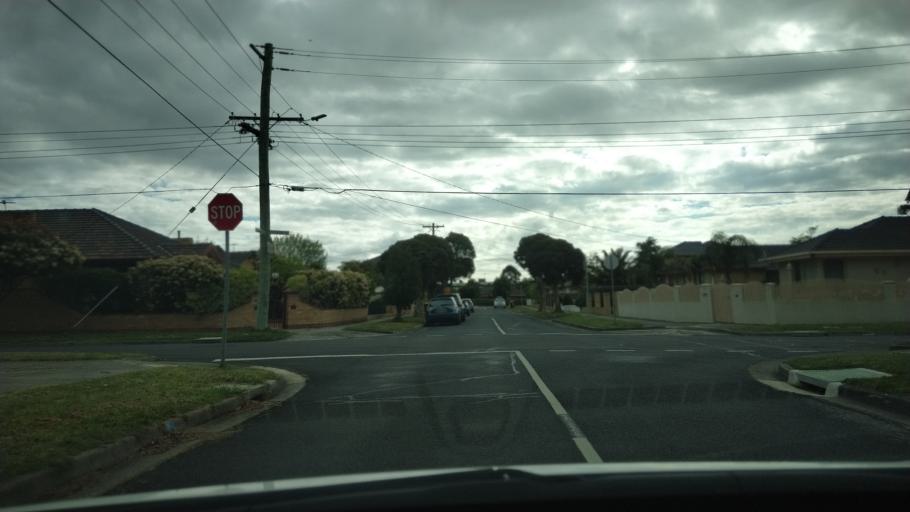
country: AU
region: Victoria
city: Highett
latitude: -37.9603
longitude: 145.0614
